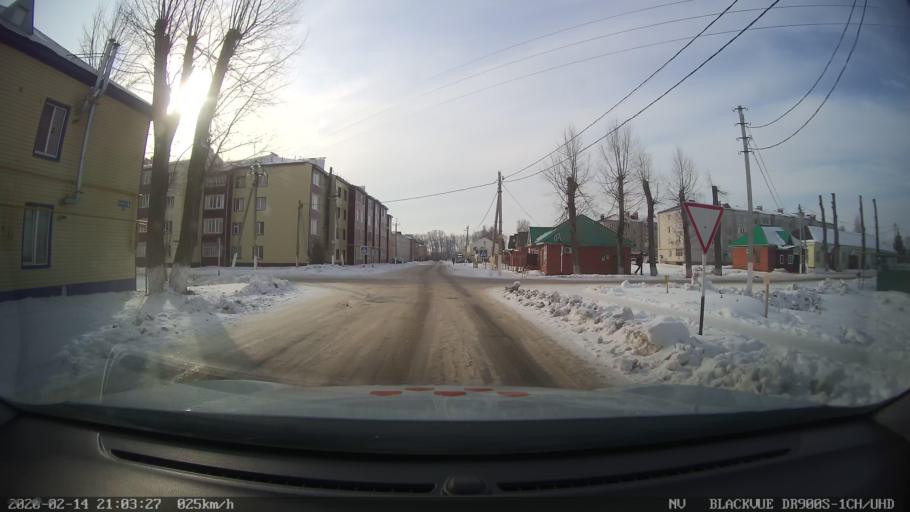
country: RU
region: Tatarstan
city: Kuybyshevskiy Zaton
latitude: 55.1567
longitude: 49.1758
